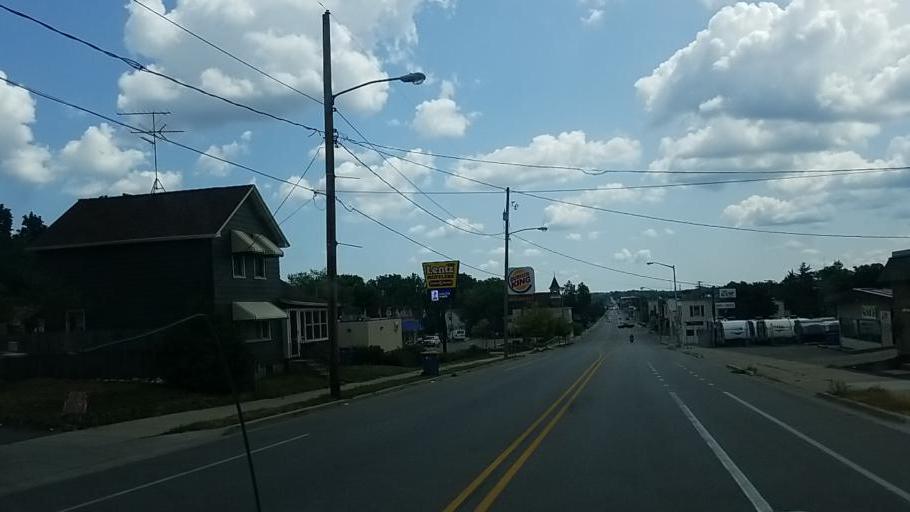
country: US
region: Michigan
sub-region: Kent County
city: Grand Rapids
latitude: 42.9856
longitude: -85.6997
